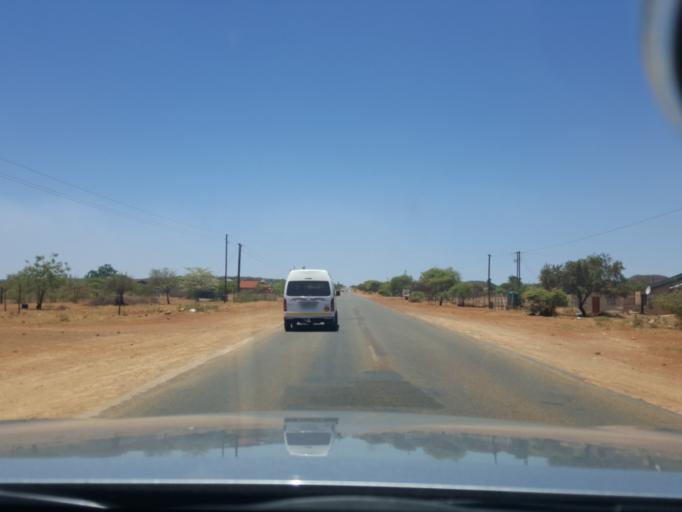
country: ZA
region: North-West
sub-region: Ngaka Modiri Molema District Municipality
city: Zeerust
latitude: -25.4442
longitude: 25.9649
